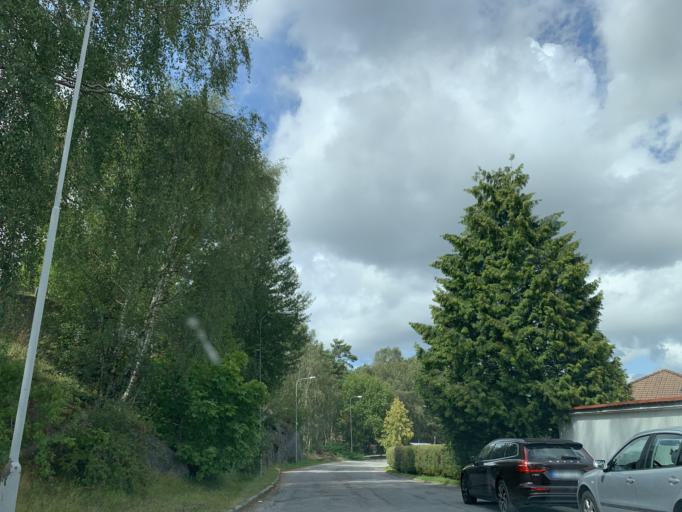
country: SE
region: Vaestra Goetaland
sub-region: Goteborg
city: Eriksbo
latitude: 57.7596
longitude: 12.0644
